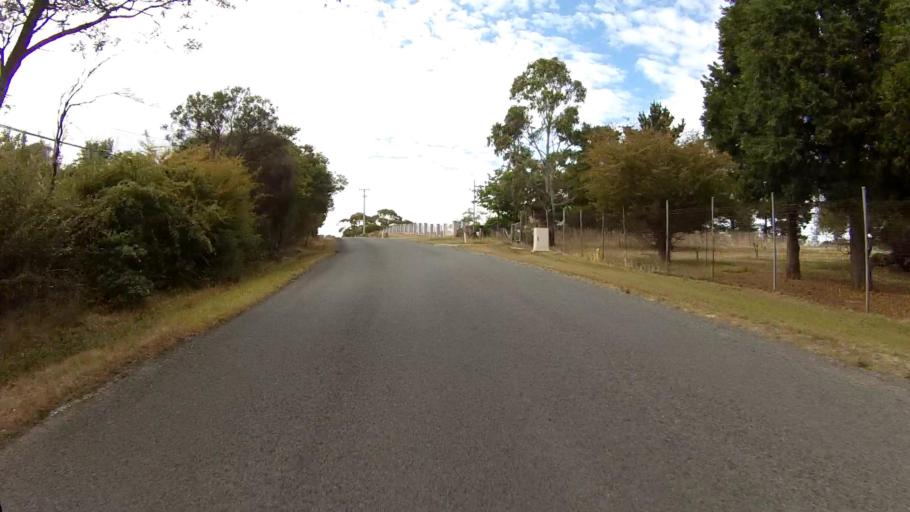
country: AU
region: Tasmania
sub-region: Glenorchy
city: Goodwood
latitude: -42.7995
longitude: 147.2896
